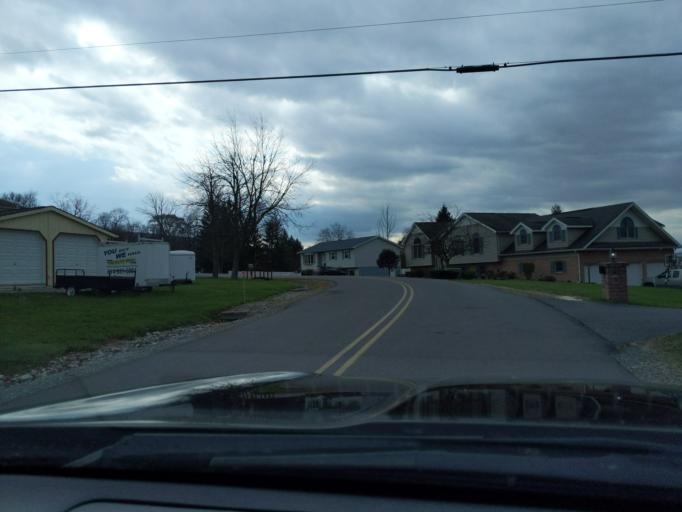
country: US
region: Pennsylvania
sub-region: Blair County
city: Greenwood
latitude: 40.5340
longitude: -78.3654
